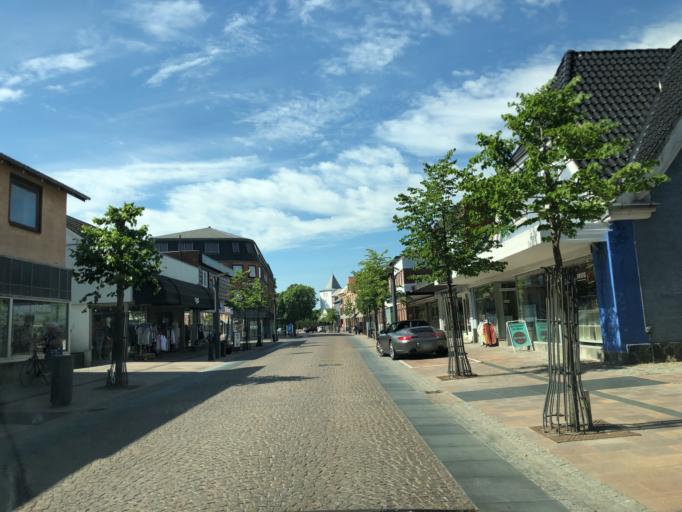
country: DK
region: Central Jutland
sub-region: Ikast-Brande Kommune
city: Brande
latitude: 55.9435
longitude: 9.1271
